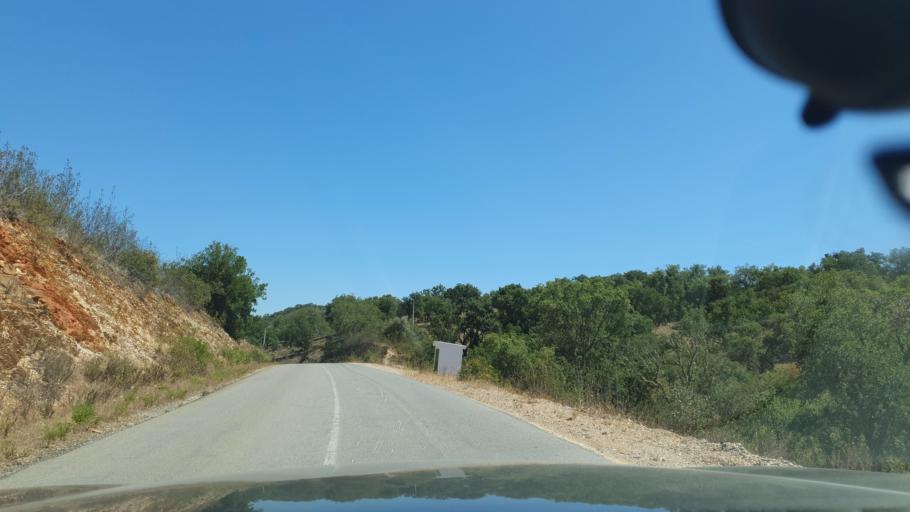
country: PT
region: Beja
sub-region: Odemira
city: Odemira
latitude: 37.5374
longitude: -8.4649
